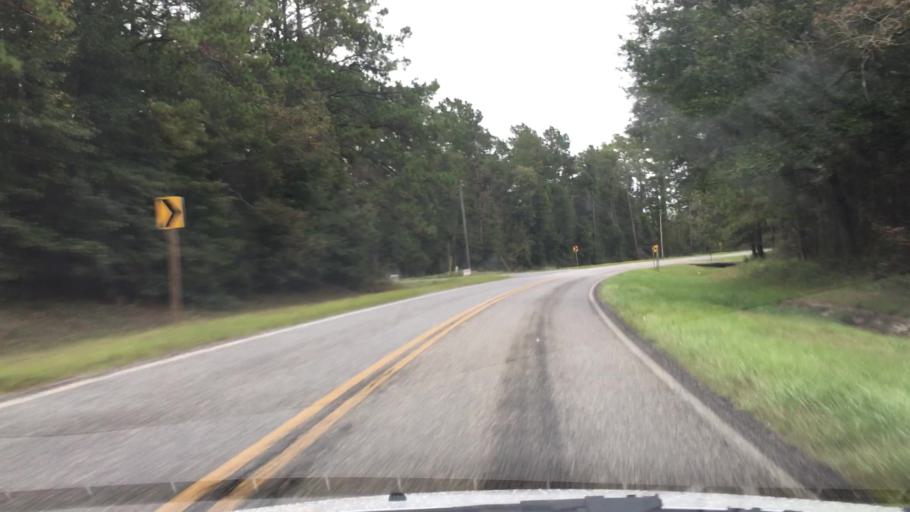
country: US
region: Georgia
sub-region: Grady County
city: Cairo
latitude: 30.8718
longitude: -84.2488
